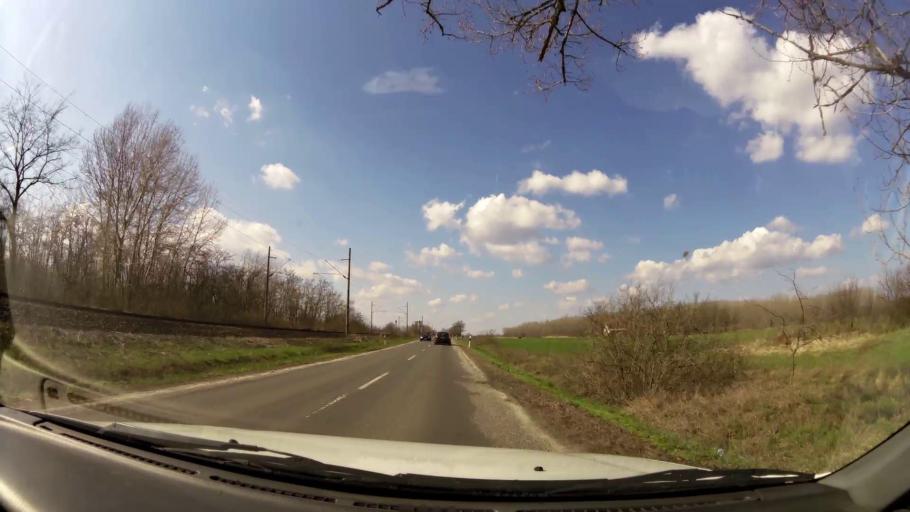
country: HU
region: Pest
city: Farmos
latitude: 47.3765
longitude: 19.7930
